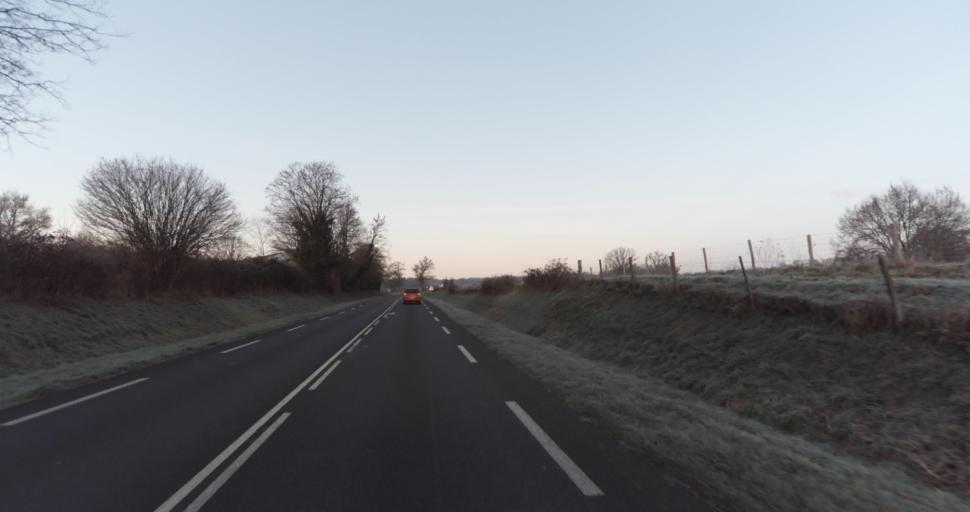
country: FR
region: Limousin
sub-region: Departement de la Haute-Vienne
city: Isle
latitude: 45.8208
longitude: 1.2033
